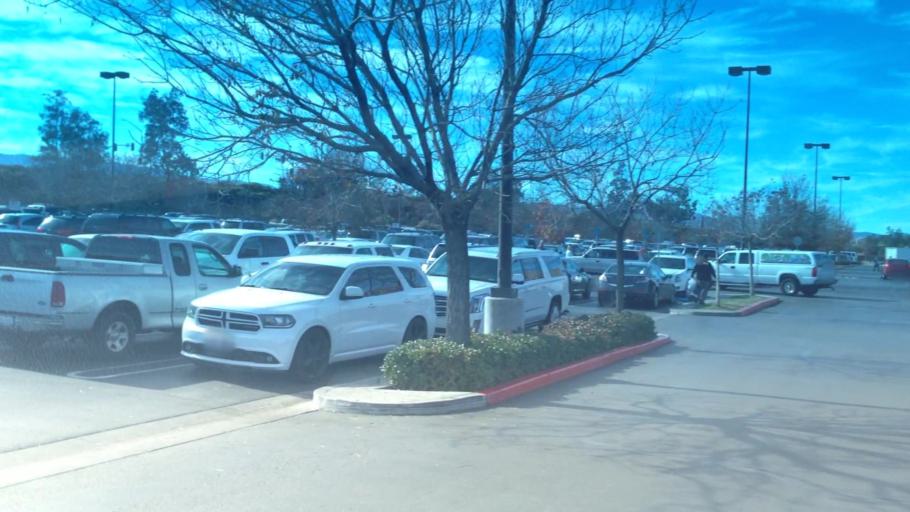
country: US
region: California
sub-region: Los Angeles County
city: Lancaster
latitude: 34.6614
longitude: -118.1505
